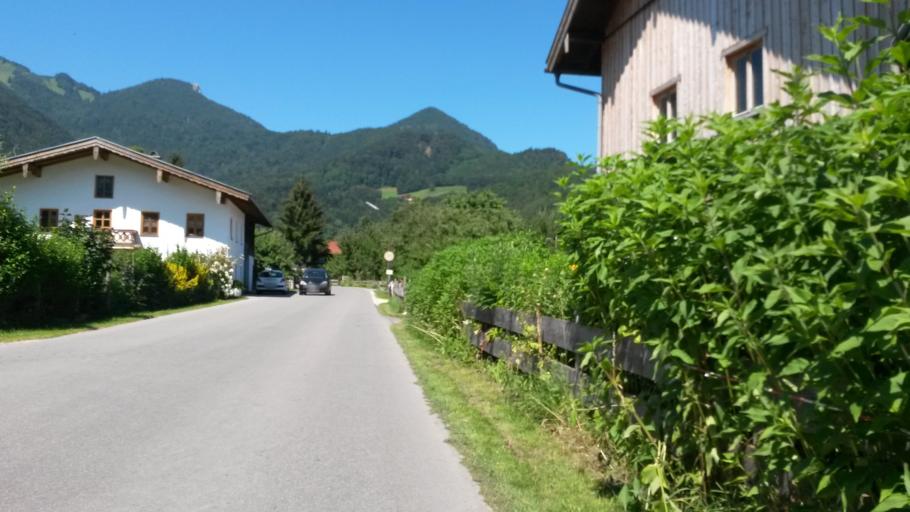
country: DE
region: Bavaria
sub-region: Upper Bavaria
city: Marquartstein
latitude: 47.7636
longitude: 12.4508
